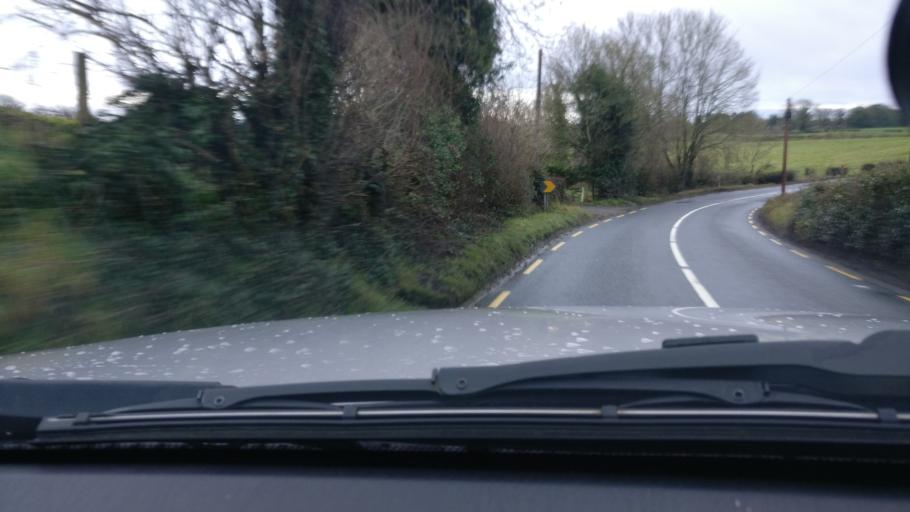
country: IE
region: Leinster
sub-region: An Longfort
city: Granard
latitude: 53.8130
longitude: -7.3709
